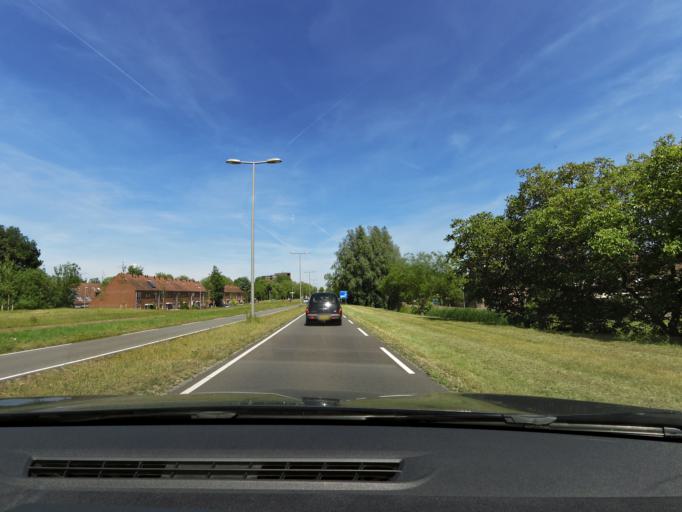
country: NL
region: South Holland
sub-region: Gemeente Spijkenisse
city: Spijkenisse
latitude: 51.8644
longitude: 4.3604
